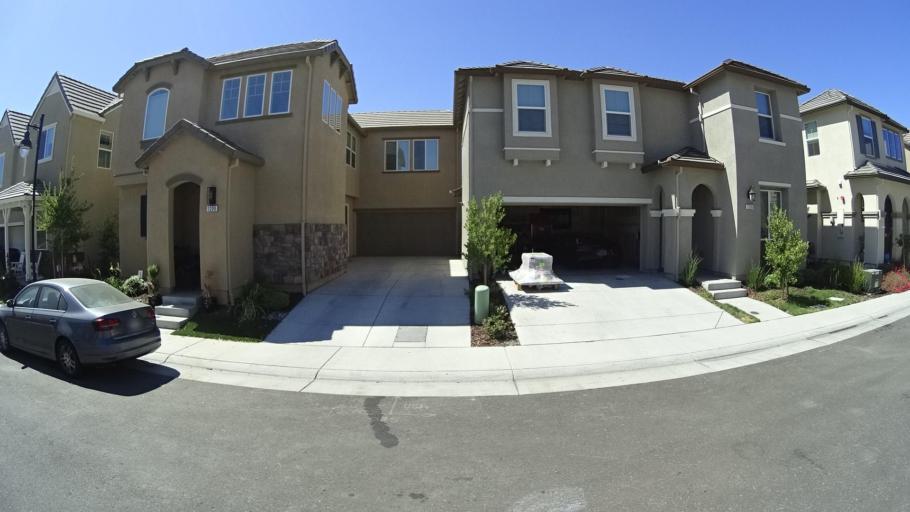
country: US
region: California
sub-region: Placer County
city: Lincoln
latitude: 38.8275
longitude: -121.2936
